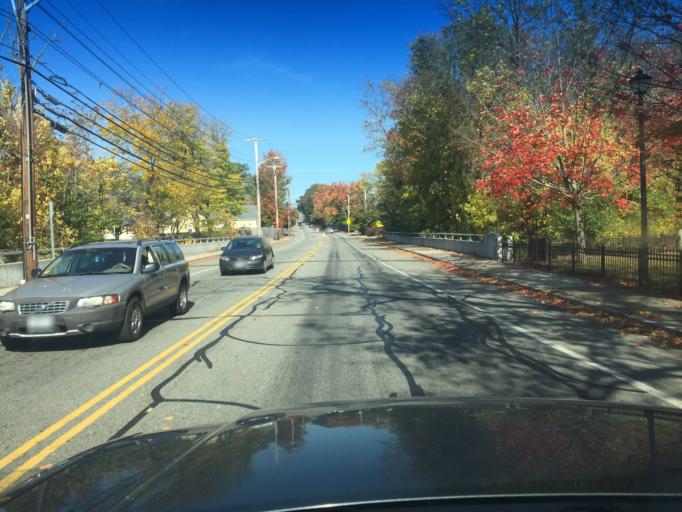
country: US
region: Rhode Island
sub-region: Providence County
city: East Providence
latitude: 41.8332
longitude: -71.3602
